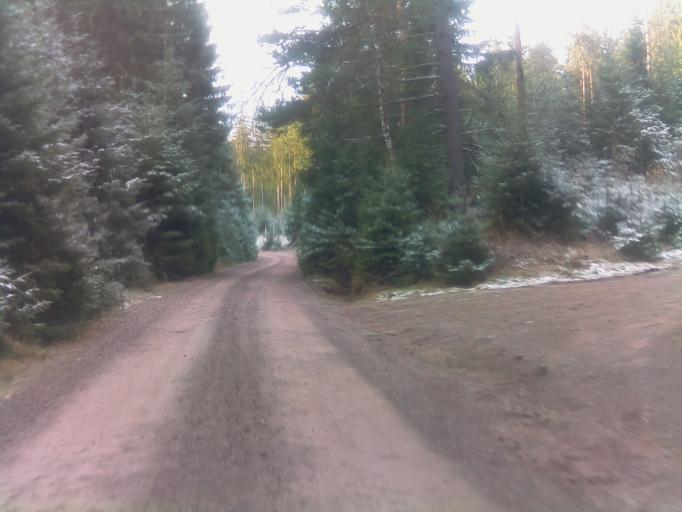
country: DE
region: Thuringia
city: Georgenthal
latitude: 50.8013
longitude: 10.6701
